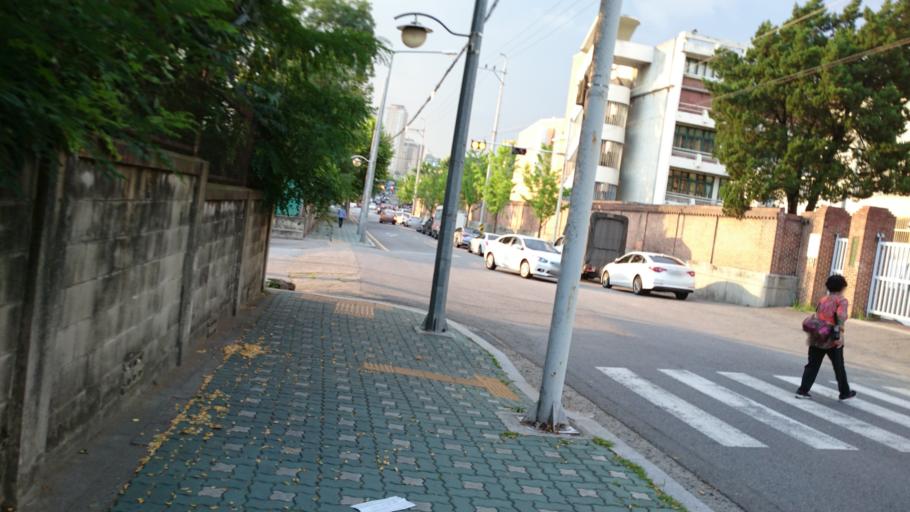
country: KR
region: Seoul
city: Seoul
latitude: 37.5446
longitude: 126.9790
